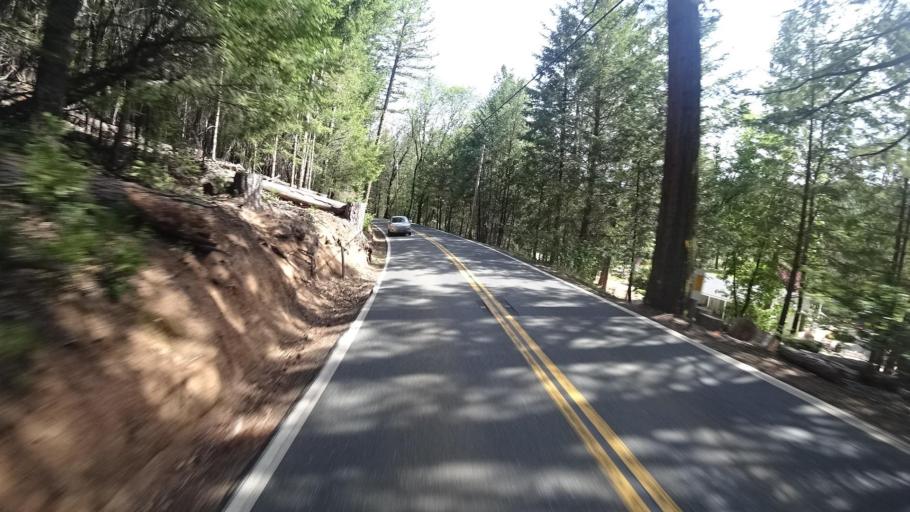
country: US
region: California
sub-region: Lake County
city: Cobb
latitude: 38.8841
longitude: -122.7276
